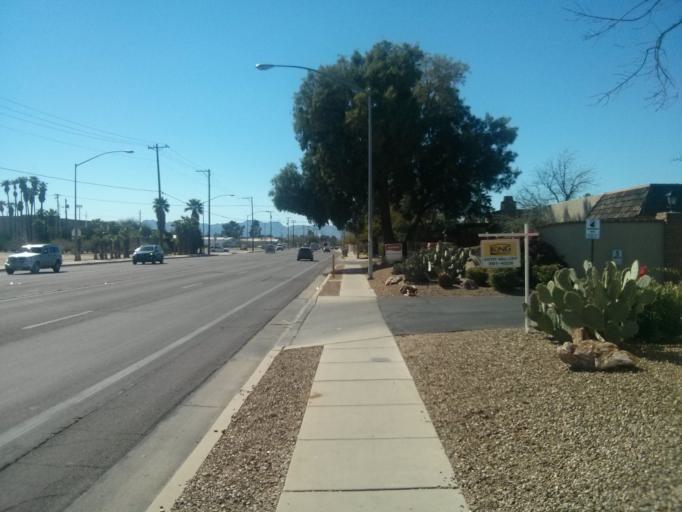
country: US
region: Arizona
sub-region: Pima County
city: Catalina Foothills
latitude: 32.2723
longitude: -110.9487
